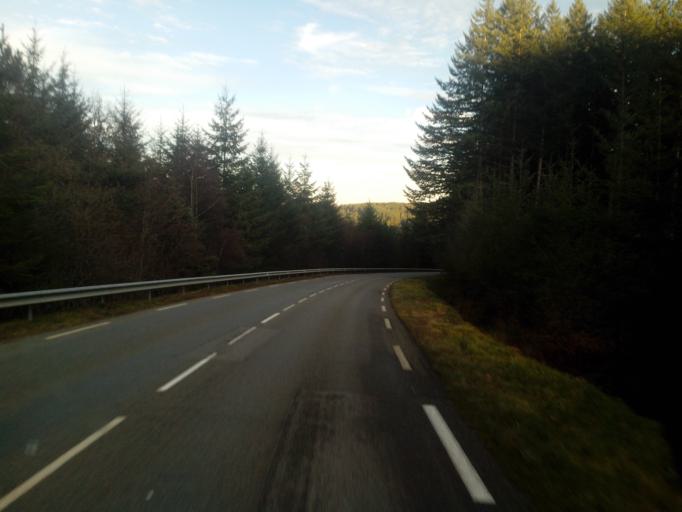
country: FR
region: Limousin
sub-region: Departement de la Correze
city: Meymac
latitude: 45.5797
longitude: 2.1154
